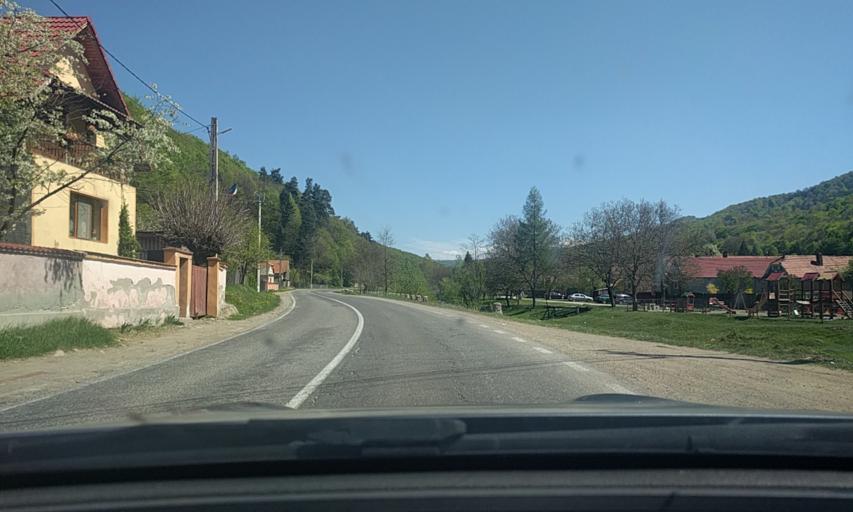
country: RO
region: Brasov
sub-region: Comuna Teliu
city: Teliu
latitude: 45.6890
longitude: 25.8890
